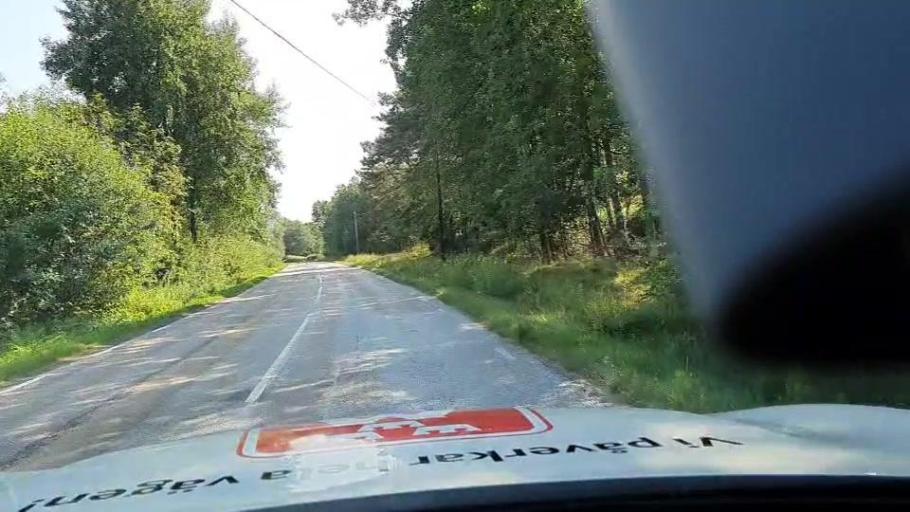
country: SE
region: Vaestra Goetaland
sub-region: Tjorns Kommun
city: Skaerhamn
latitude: 58.1019
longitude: 11.4853
